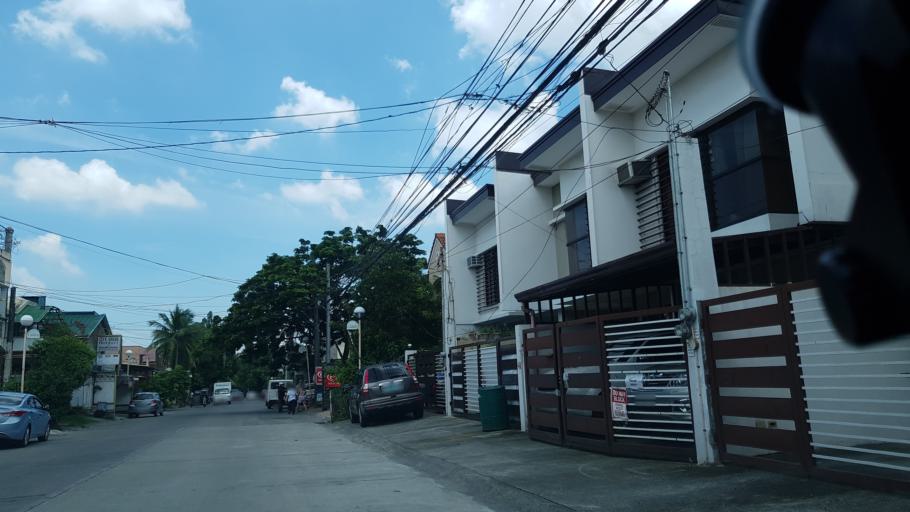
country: PH
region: Calabarzon
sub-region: Province of Rizal
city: Las Pinas
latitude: 14.4309
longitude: 120.9891
